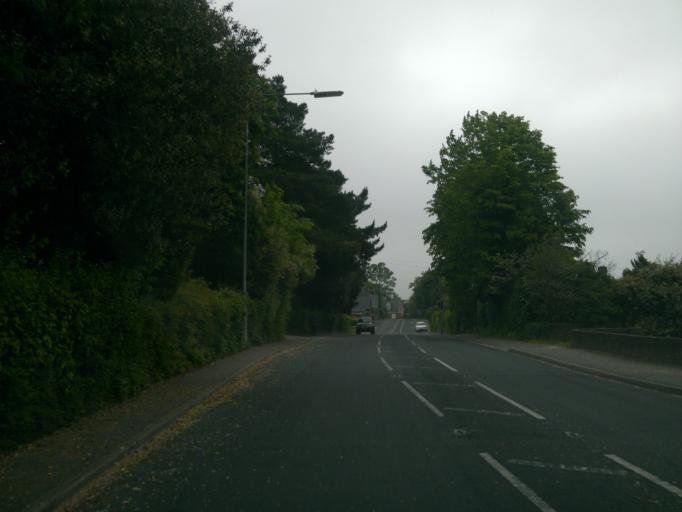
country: GB
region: England
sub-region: Essex
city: Colchester
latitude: 51.9063
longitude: 0.8800
